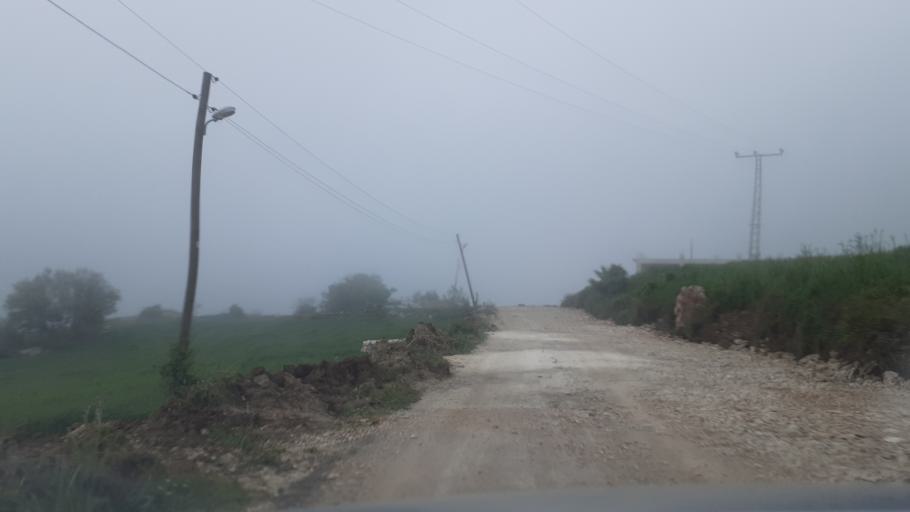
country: TR
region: Hatay
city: Yeditepe
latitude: 35.9715
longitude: 36.0021
